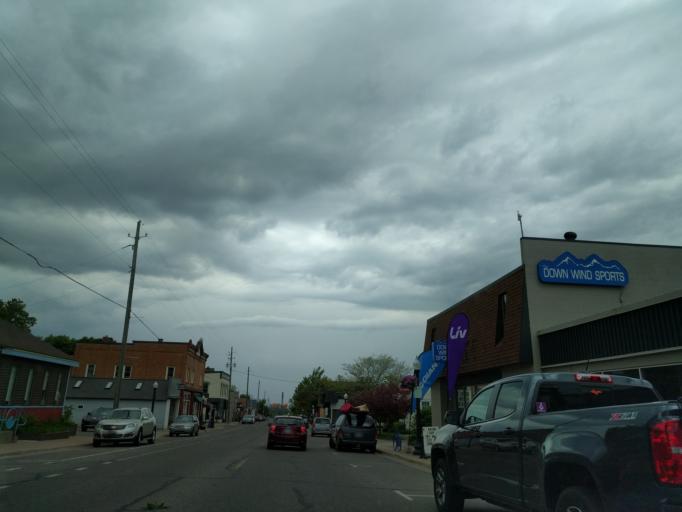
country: US
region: Michigan
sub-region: Marquette County
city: Marquette
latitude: 46.5474
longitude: -87.3947
